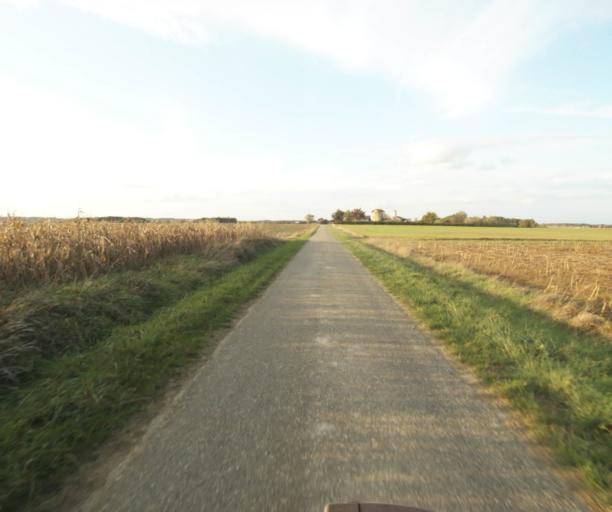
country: FR
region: Midi-Pyrenees
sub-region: Departement du Tarn-et-Garonne
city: Verdun-sur-Garonne
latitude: 43.8291
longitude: 1.1604
